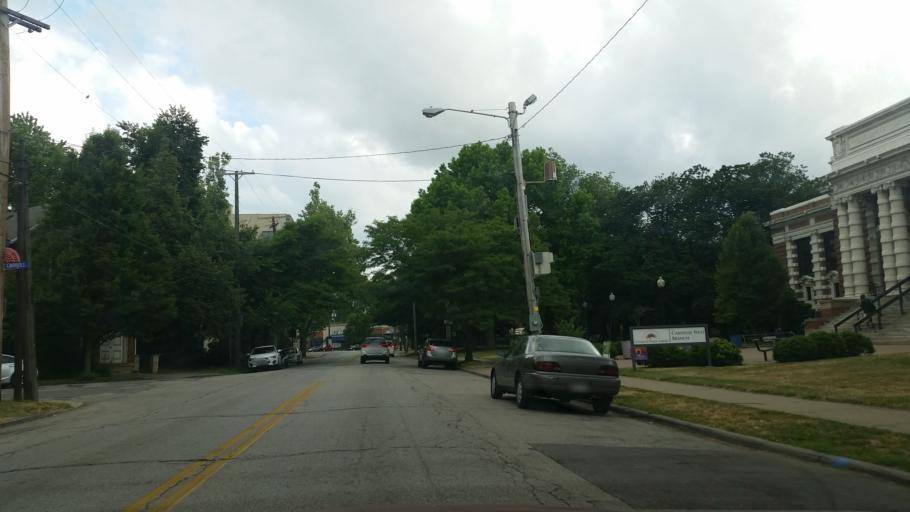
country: US
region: Ohio
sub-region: Cuyahoga County
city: Cleveland
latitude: 41.4827
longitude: -81.7107
